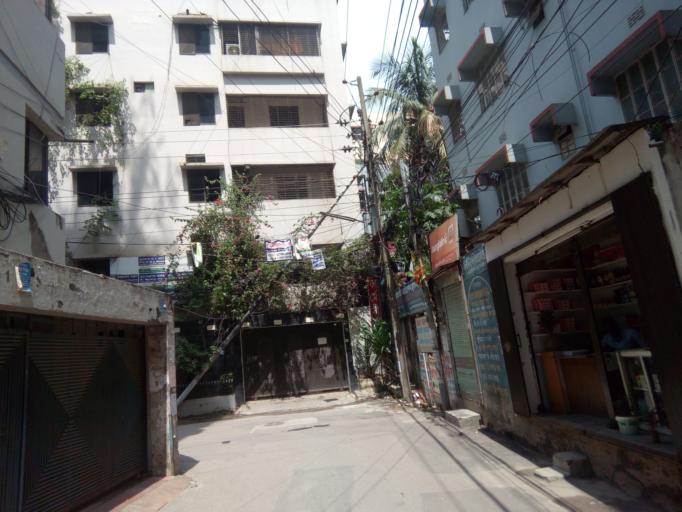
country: BD
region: Dhaka
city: Azimpur
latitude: 23.7491
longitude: 90.3829
